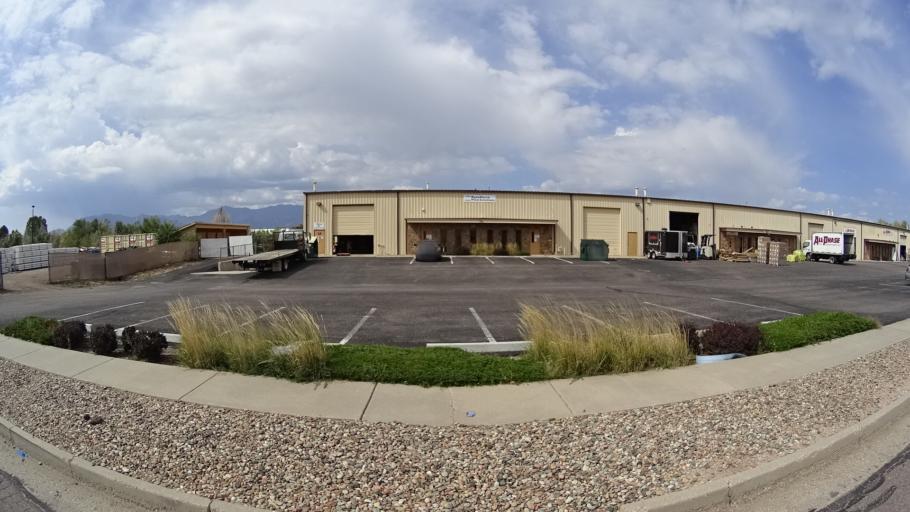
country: US
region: Colorado
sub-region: El Paso County
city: Cimarron Hills
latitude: 38.8432
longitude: -104.7337
